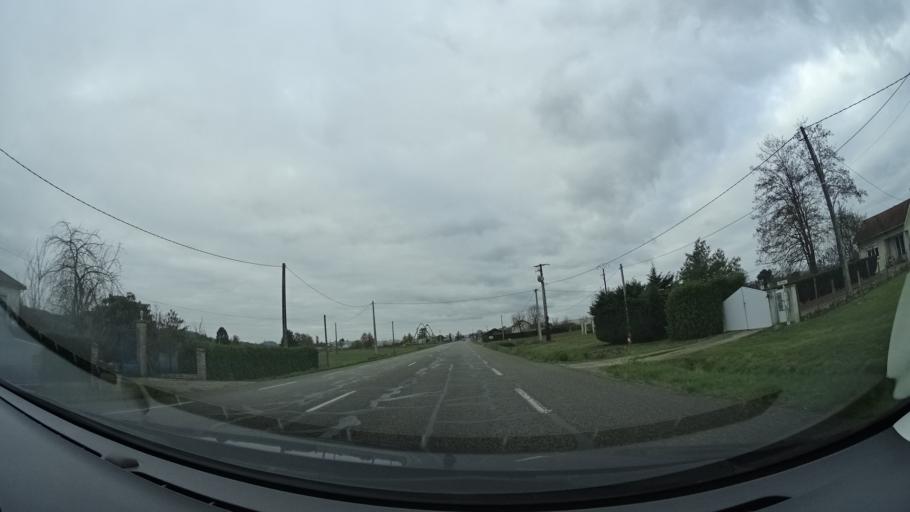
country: FR
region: Aquitaine
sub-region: Departement du Lot-et-Garonne
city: Sainte-Livrade-sur-Lot
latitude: 44.4008
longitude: 0.6268
